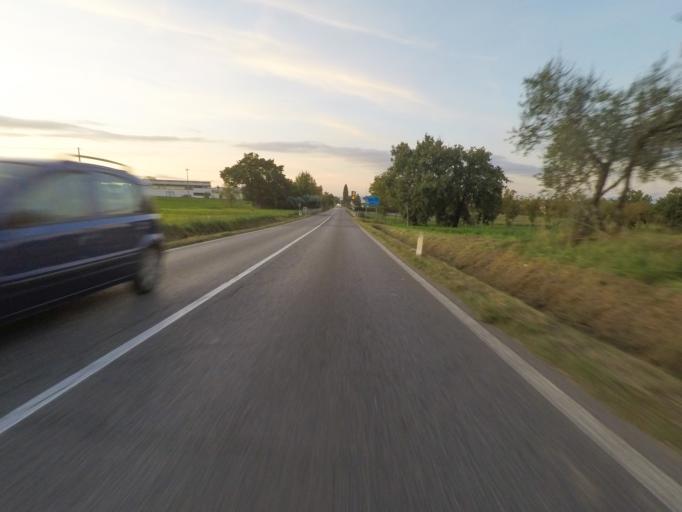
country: IT
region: Tuscany
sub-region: Provincia di Siena
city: Torrita di Siena
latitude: 43.1774
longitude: 11.7724
